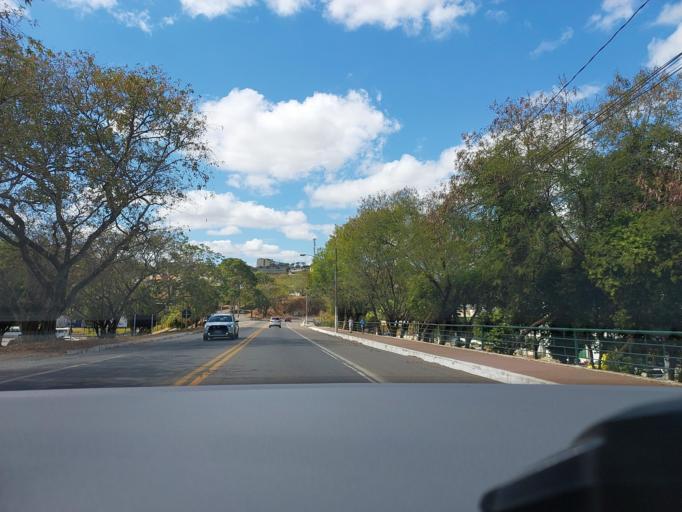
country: BR
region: Minas Gerais
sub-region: Muriae
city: Muriae
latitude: -21.1268
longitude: -42.3721
